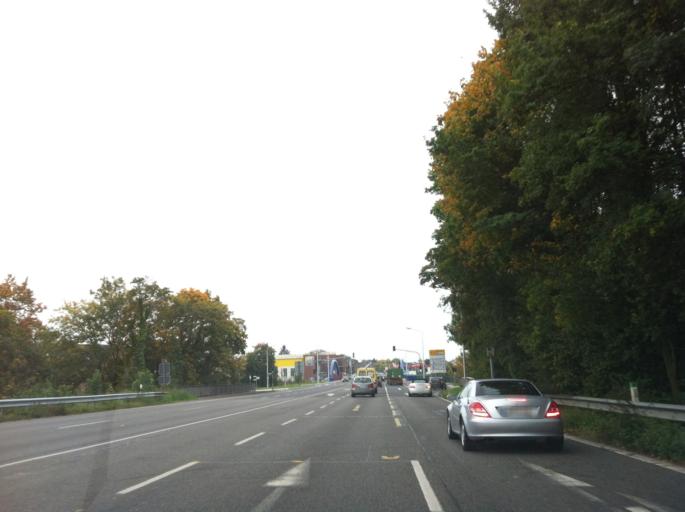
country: DE
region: North Rhine-Westphalia
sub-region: Regierungsbezirk Koln
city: Dueren
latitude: 50.8167
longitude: 6.4874
